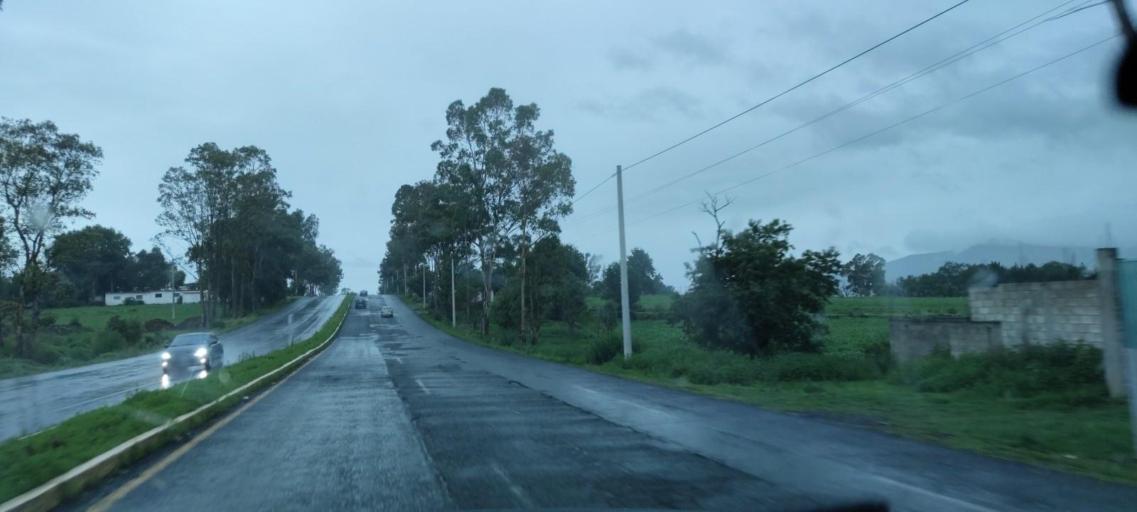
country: MX
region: Mexico
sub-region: Jilotepec
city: Doxhicho
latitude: 19.9142
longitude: -99.6027
